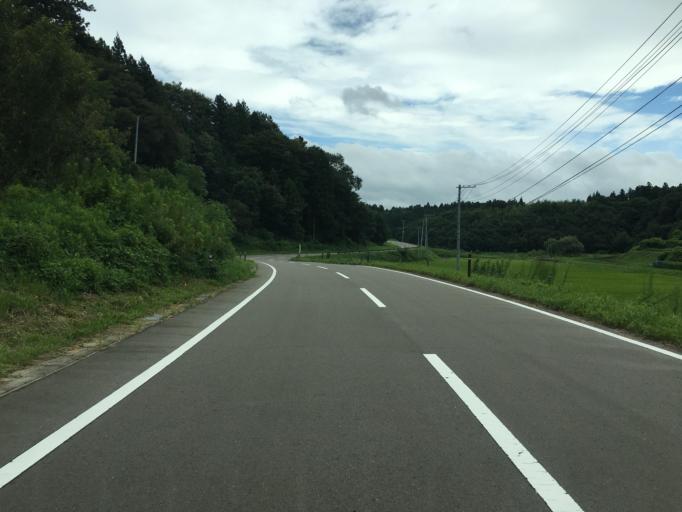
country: JP
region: Fukushima
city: Nihommatsu
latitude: 37.6283
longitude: 140.4501
